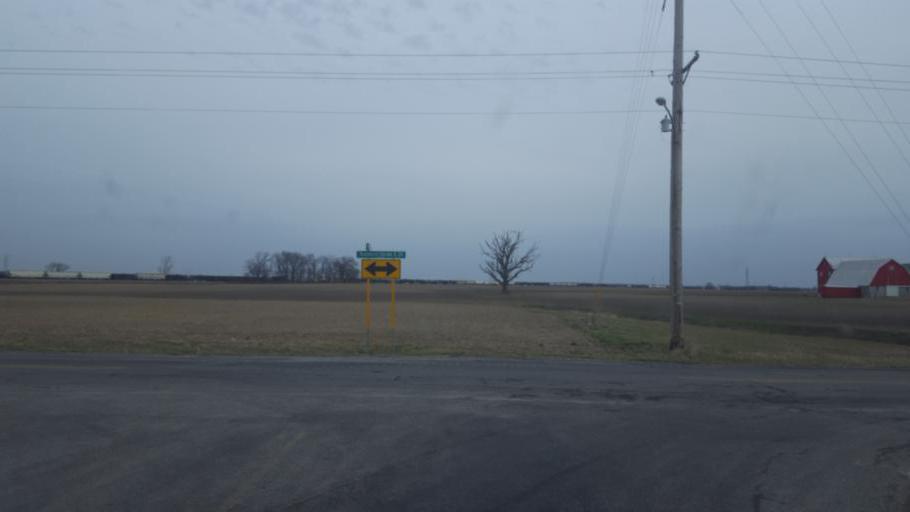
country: US
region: Ohio
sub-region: Marion County
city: Marion
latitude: 40.6735
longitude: -83.0730
